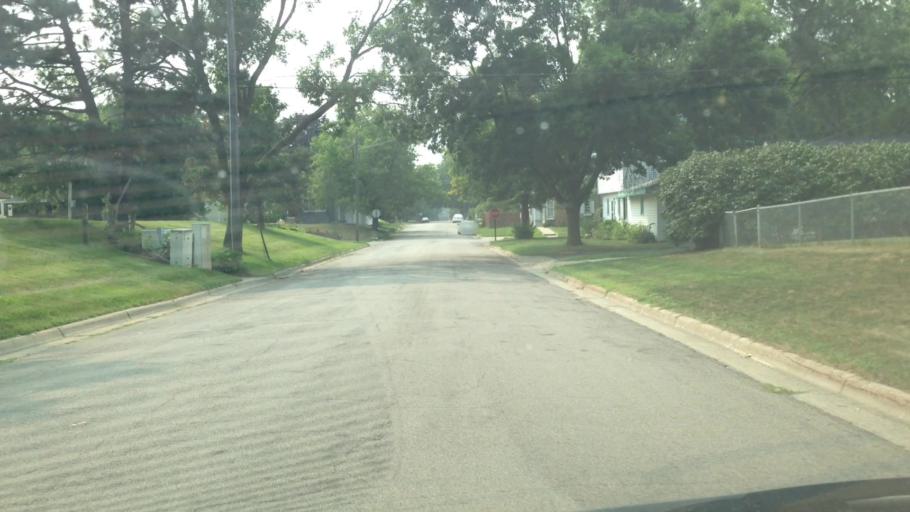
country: US
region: Minnesota
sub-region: Hennepin County
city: Saint Louis Park
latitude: 44.9514
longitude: -93.3672
